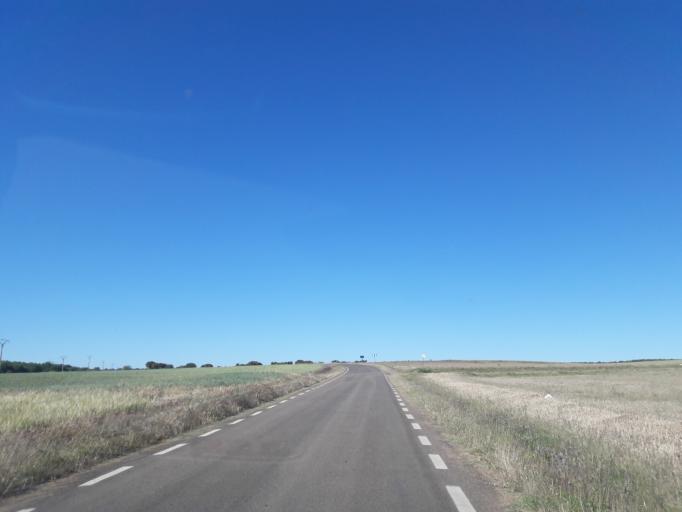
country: ES
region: Castille and Leon
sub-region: Provincia de Salamanca
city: Florida de Liebana
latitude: 41.0199
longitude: -5.7661
